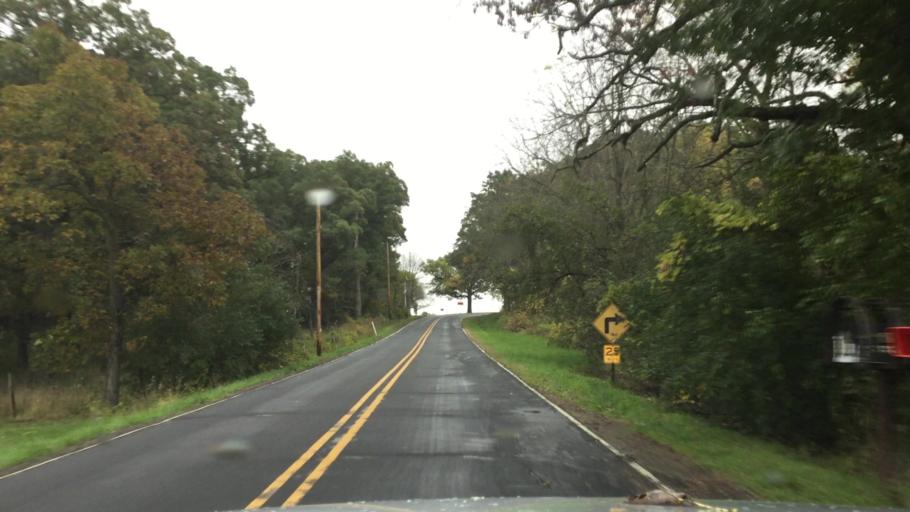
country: US
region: Wisconsin
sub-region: Racine County
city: Waterford
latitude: 42.7602
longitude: -88.1628
